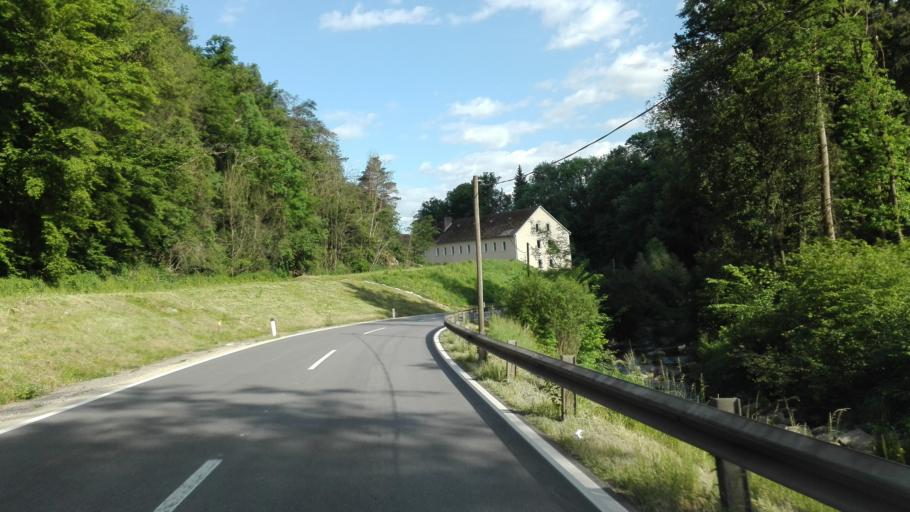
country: AT
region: Upper Austria
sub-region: Politischer Bezirk Urfahr-Umgebung
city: Engerwitzdorf
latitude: 48.3394
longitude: 14.4583
